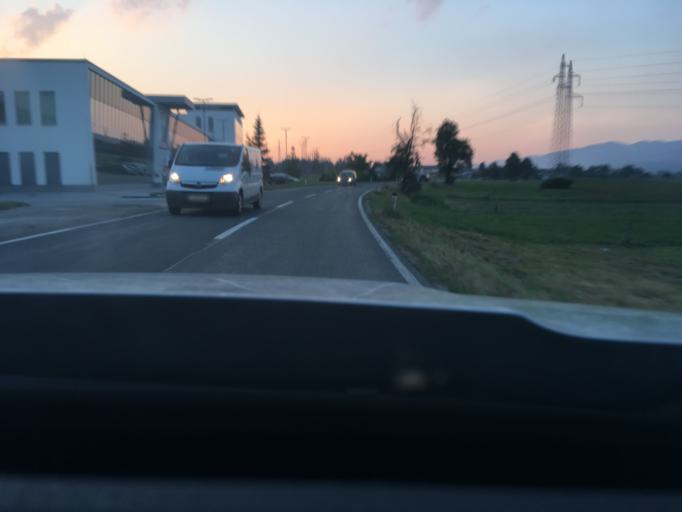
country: SI
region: Ribnica
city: Ribnica
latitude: 45.7148
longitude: 14.7473
